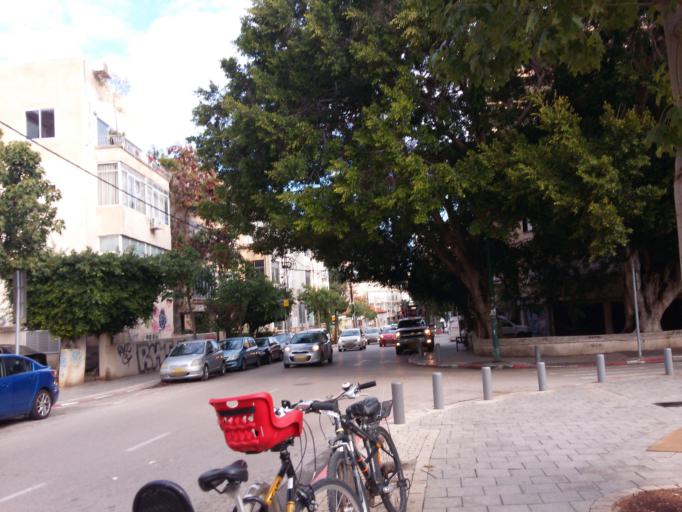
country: IL
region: Tel Aviv
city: Tel Aviv
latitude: 32.0686
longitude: 34.7804
